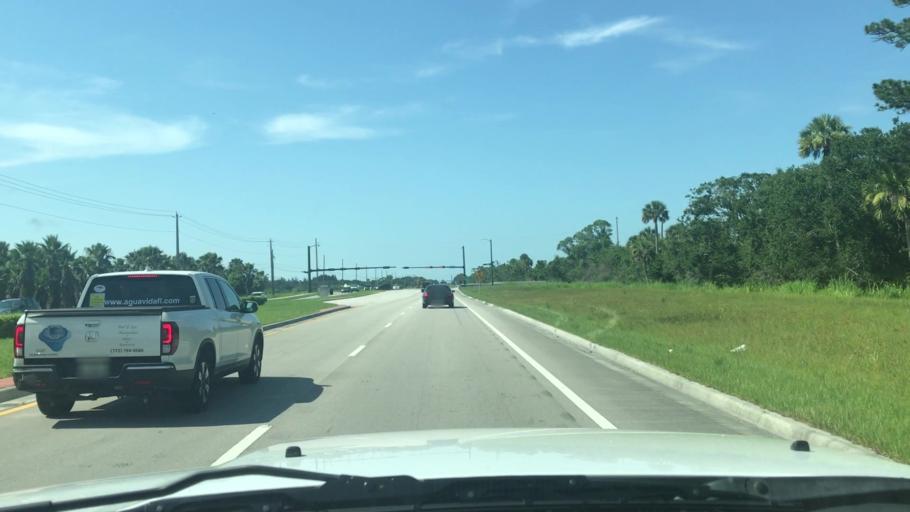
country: US
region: Florida
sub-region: Indian River County
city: West Vero Corridor
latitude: 27.6660
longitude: -80.4630
